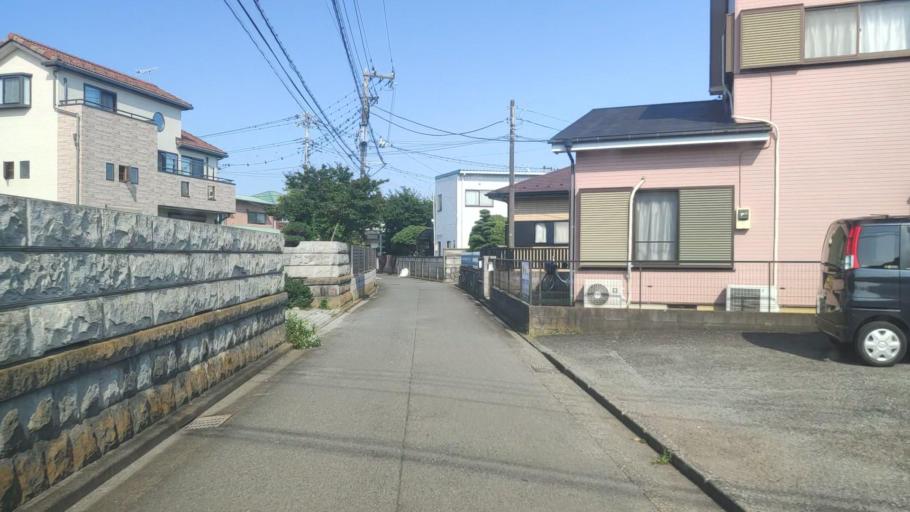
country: JP
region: Kanagawa
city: Hiratsuka
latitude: 35.3321
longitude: 139.3230
